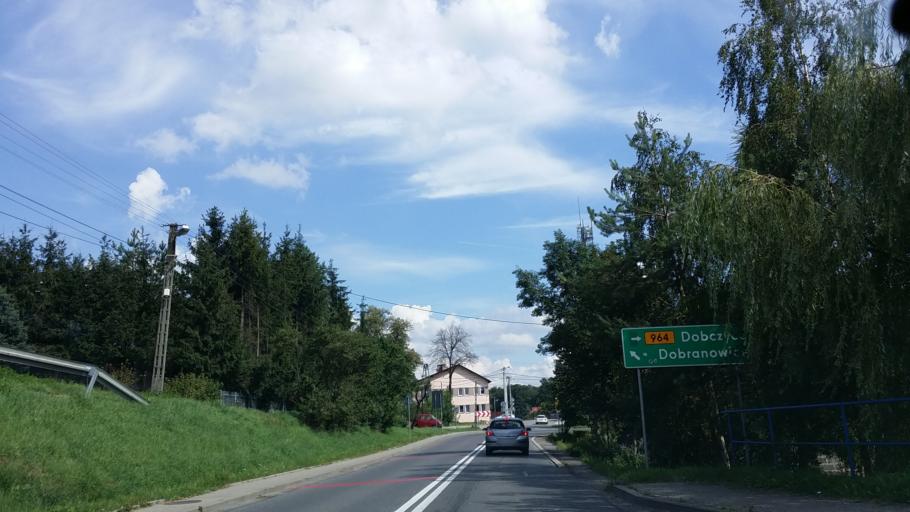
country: PL
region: Lesser Poland Voivodeship
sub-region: Powiat wielicki
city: Pawlikowice
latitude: 49.9356
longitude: 20.0615
